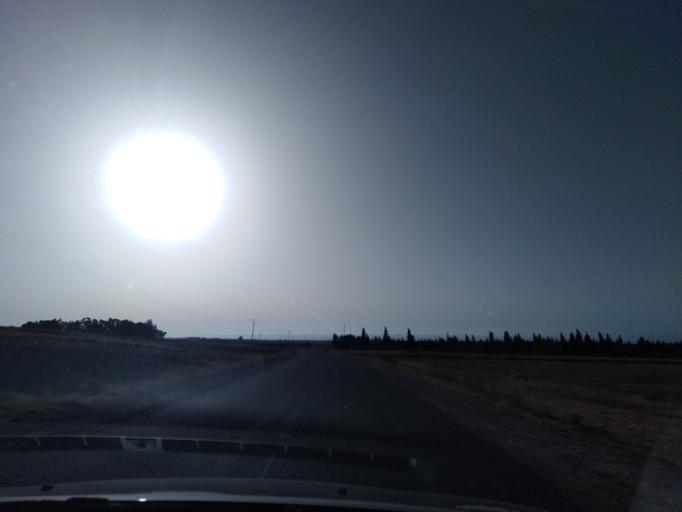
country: MA
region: Doukkala-Abda
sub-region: Safi
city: Safi
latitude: 32.4809
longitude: -8.9074
